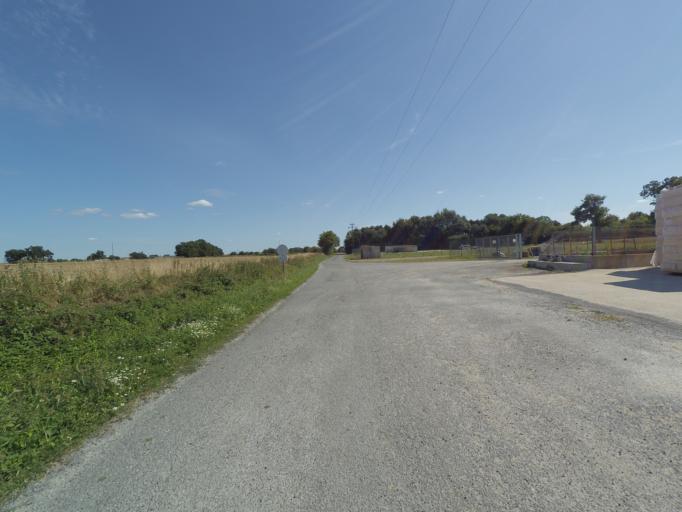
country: FR
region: Pays de la Loire
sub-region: Departement de la Vendee
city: Saint-Andre-Treize-Voies
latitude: 46.9514
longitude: -1.4112
